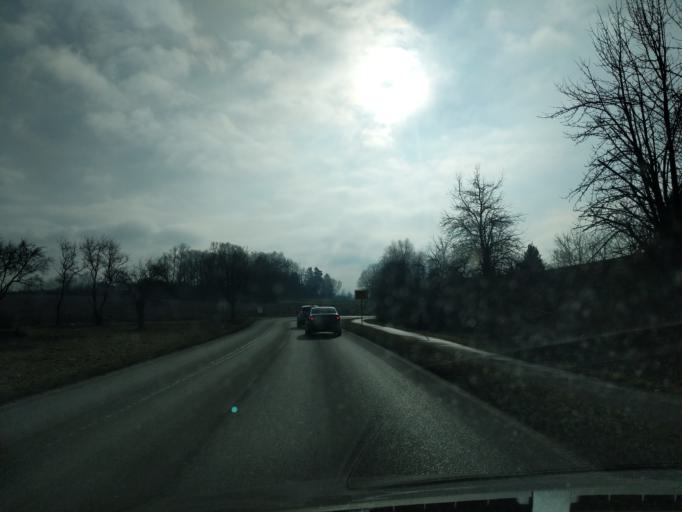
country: DE
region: Baden-Wuerttemberg
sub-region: Tuebingen Region
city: Markdorf
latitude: 47.7055
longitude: 9.4007
